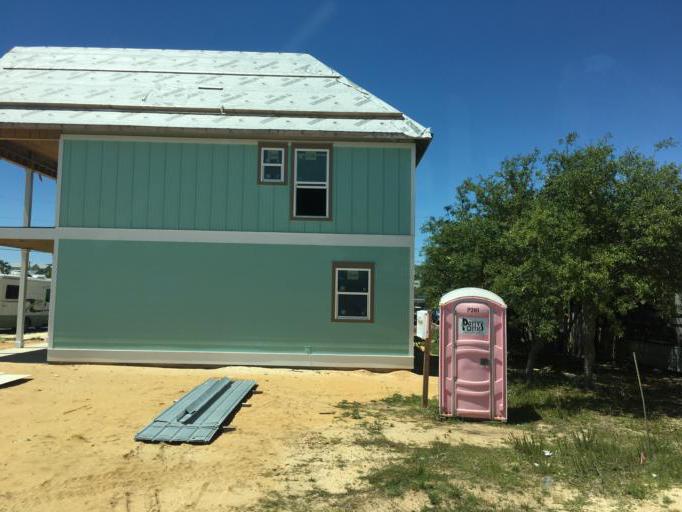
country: US
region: Florida
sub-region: Bay County
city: Laguna Beach
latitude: 30.2442
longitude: -85.9300
